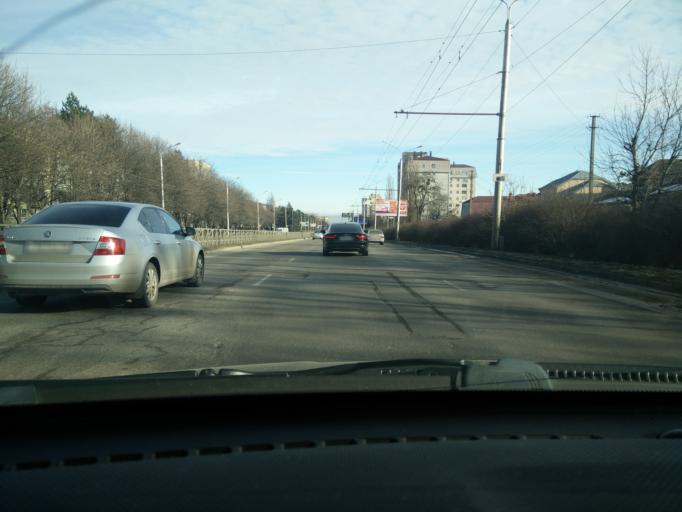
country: RU
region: Stavropol'skiy
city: Stavropol'
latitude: 45.0328
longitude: 41.9484
